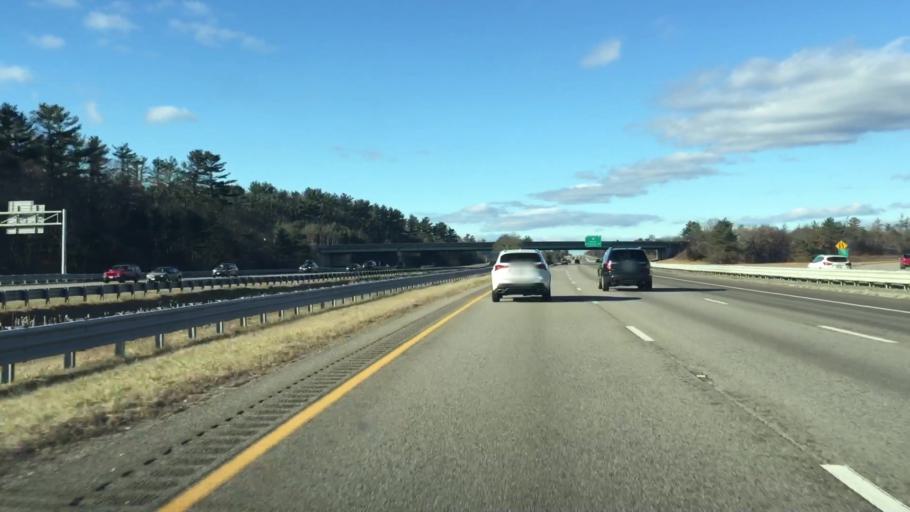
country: US
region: Massachusetts
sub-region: Bristol County
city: Mansfield Center
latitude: 42.0049
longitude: -71.2217
